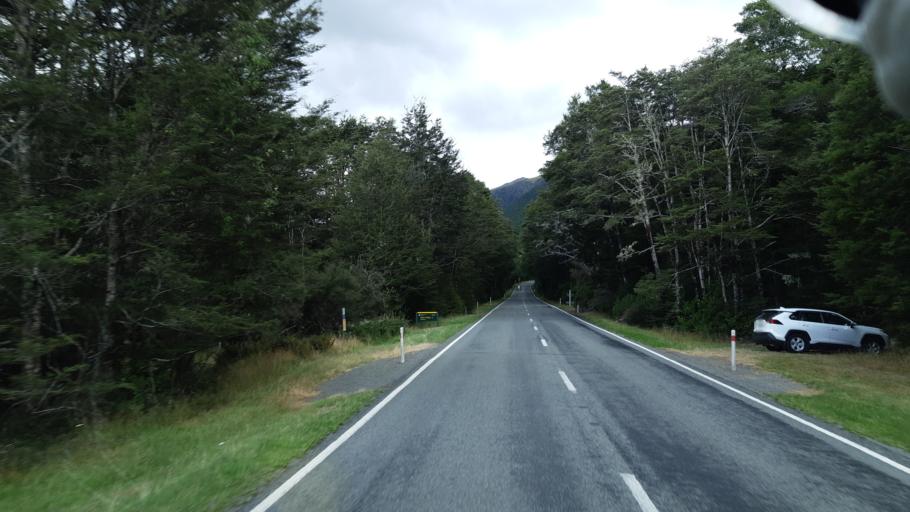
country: NZ
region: Canterbury
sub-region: Hurunui District
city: Amberley
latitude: -42.4697
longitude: 172.3974
